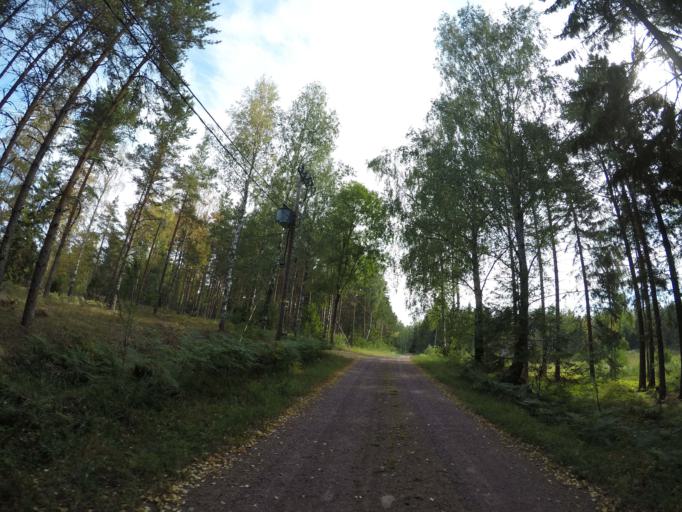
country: AX
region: Alands landsbygd
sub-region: Hammarland
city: Hammarland
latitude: 60.2244
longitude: 19.8321
